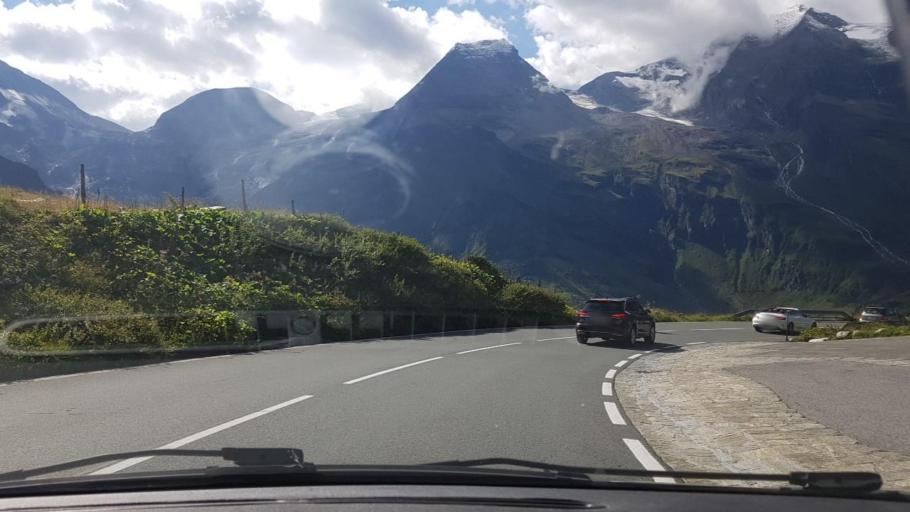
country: AT
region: Carinthia
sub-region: Politischer Bezirk Spittal an der Drau
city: Heiligenblut
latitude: 47.1218
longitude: 12.8099
